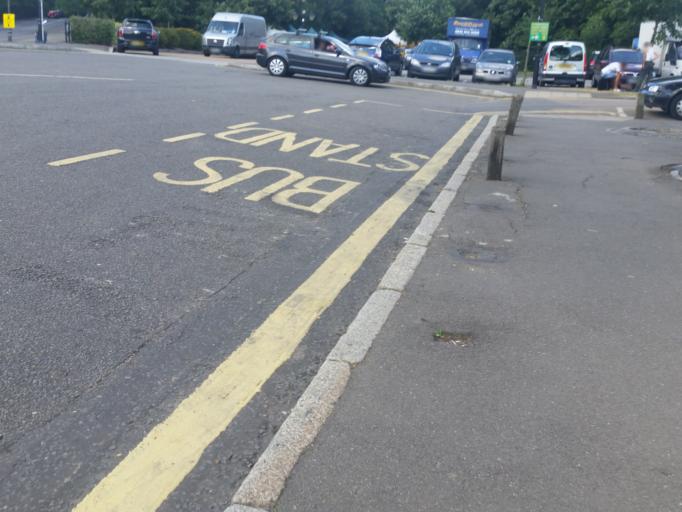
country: GB
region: England
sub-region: Greater London
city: Crouch End
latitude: 51.5879
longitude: -0.1335
